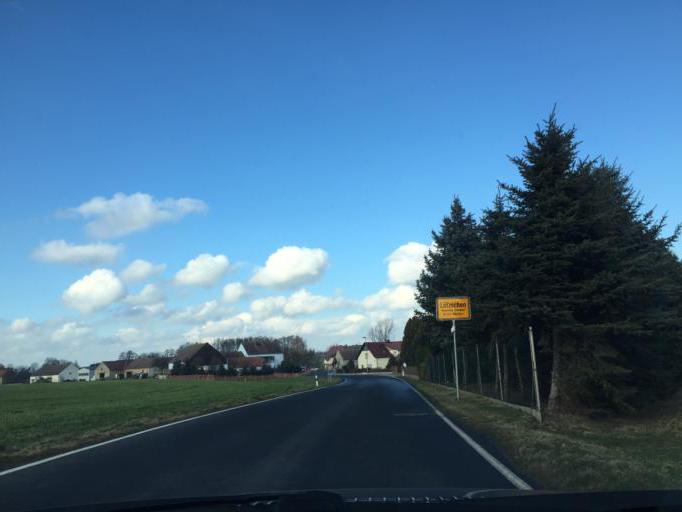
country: DE
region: Saxony
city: Thiendorf
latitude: 51.2762
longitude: 13.7492
